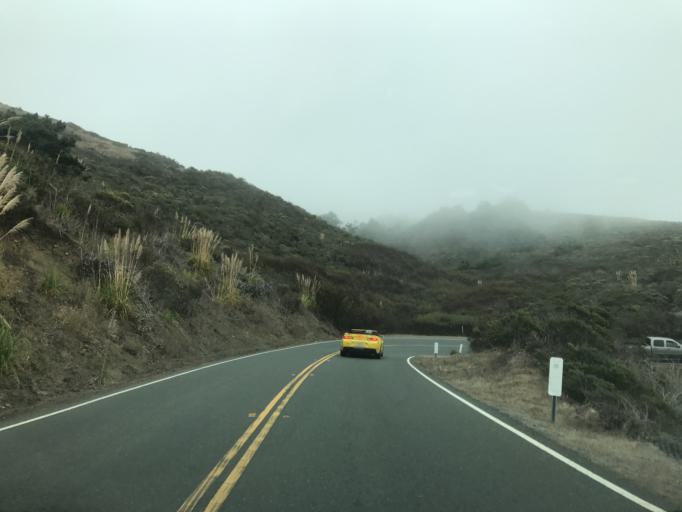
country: US
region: California
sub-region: Sonoma County
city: Monte Rio
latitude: 38.4552
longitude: -123.1336
